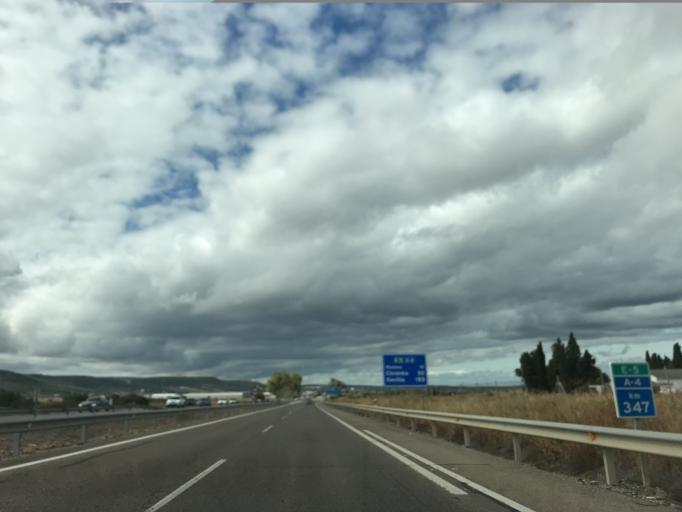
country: ES
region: Andalusia
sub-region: Province of Cordoba
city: Villa del Rio
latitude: 37.9889
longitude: -4.2643
